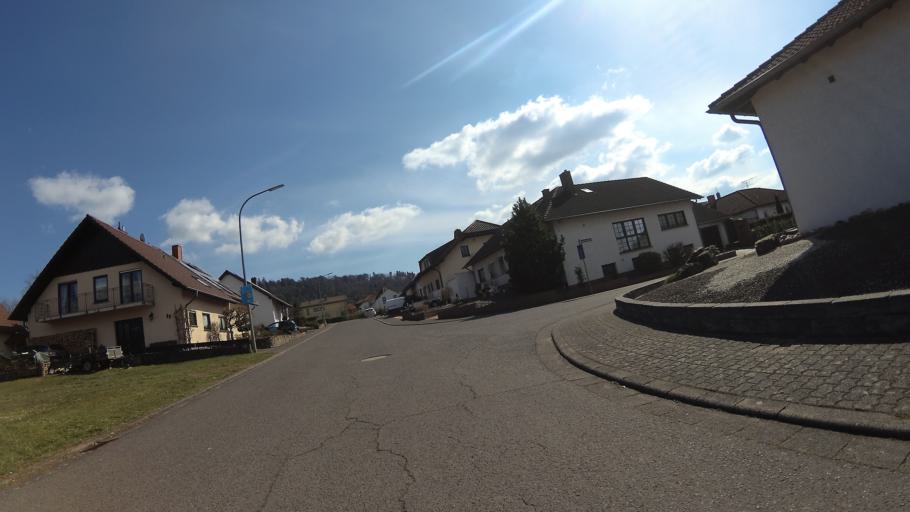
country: DE
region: Saarland
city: Rehlingen-Siersburg
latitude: 49.3609
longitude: 6.6689
